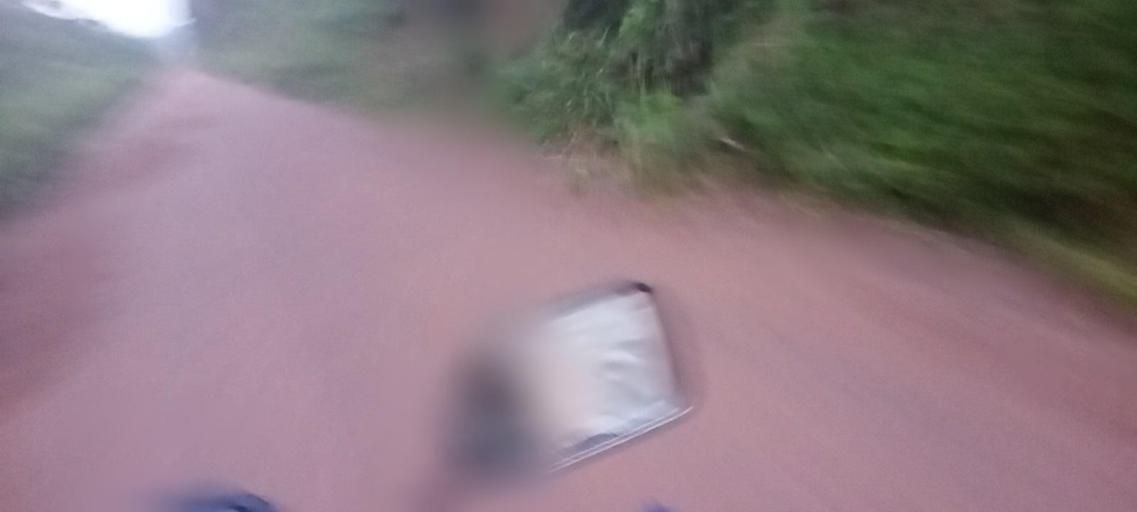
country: CD
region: Eastern Province
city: Kisangani
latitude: -0.1748
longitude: 25.7268
